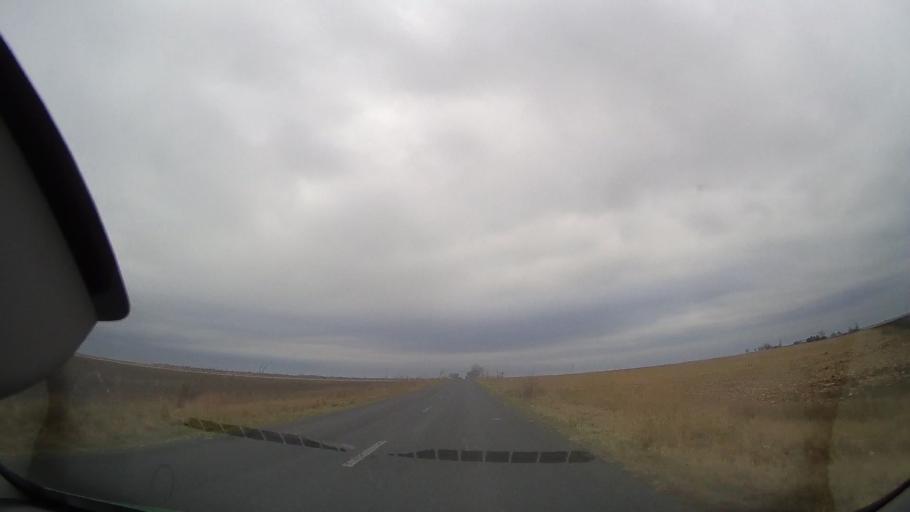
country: RO
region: Buzau
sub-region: Comuna Padina
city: Padina
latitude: 44.7935
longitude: 27.1414
